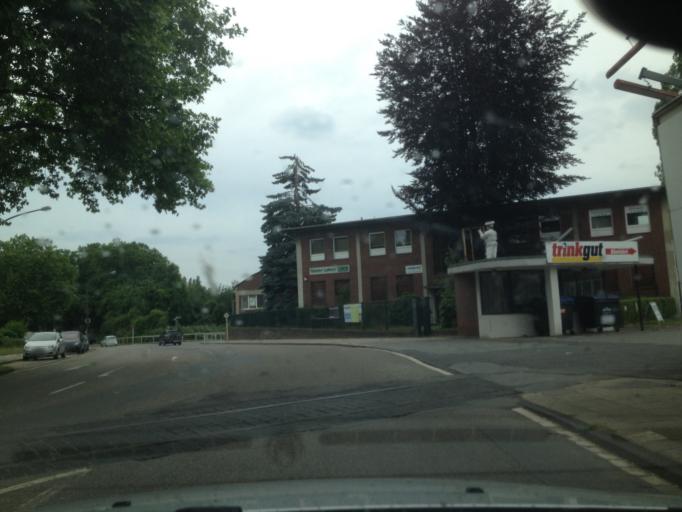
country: DE
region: North Rhine-Westphalia
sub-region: Regierungsbezirk Munster
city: Gelsenkirchen
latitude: 51.4397
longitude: 7.0937
